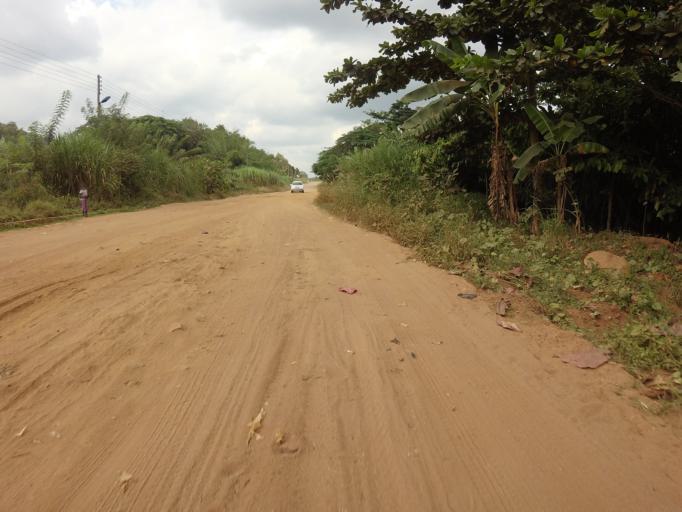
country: GH
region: Volta
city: Ho
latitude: 6.6528
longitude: 0.3425
